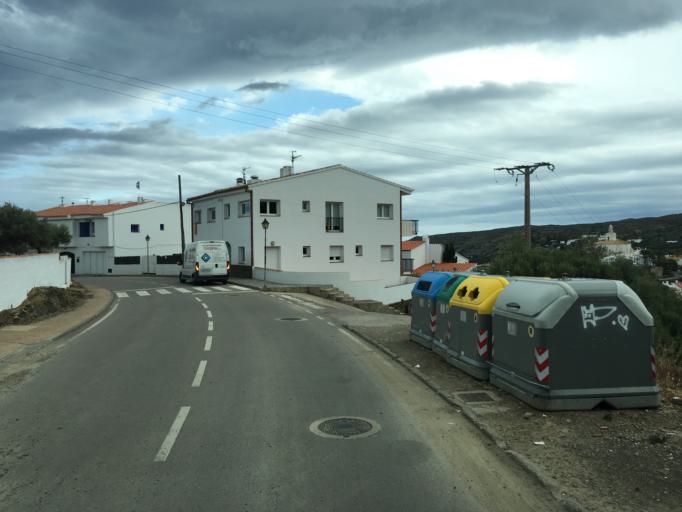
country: ES
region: Catalonia
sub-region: Provincia de Girona
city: Cadaques
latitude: 42.2925
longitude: 3.2755
